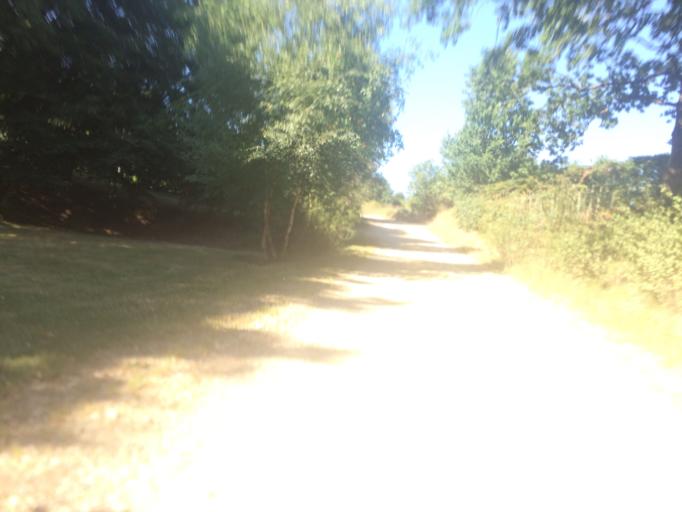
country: DK
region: Central Jutland
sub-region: Holstebro Kommune
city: Vinderup
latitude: 56.5763
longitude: 8.7262
